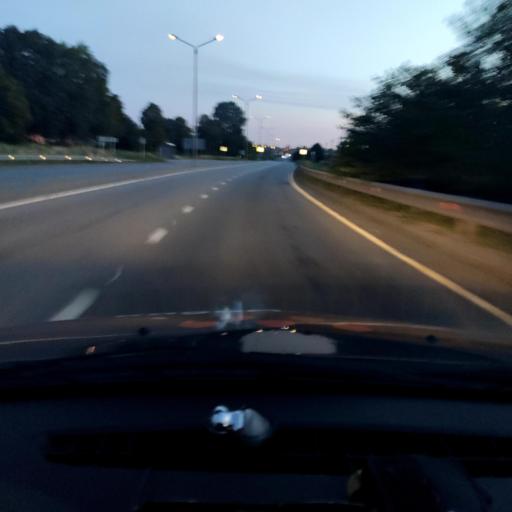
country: RU
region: Belgorod
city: Gubkin
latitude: 51.2773
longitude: 37.5929
